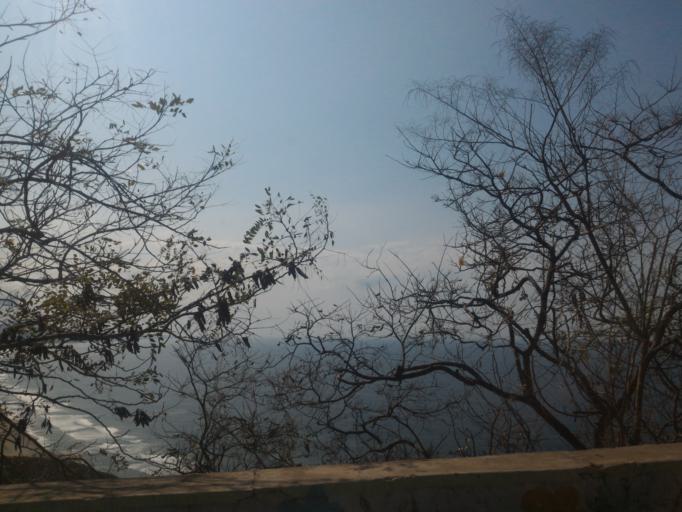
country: MX
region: Michoacan
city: Coahuayana Viejo
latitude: 18.5634
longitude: -103.6474
